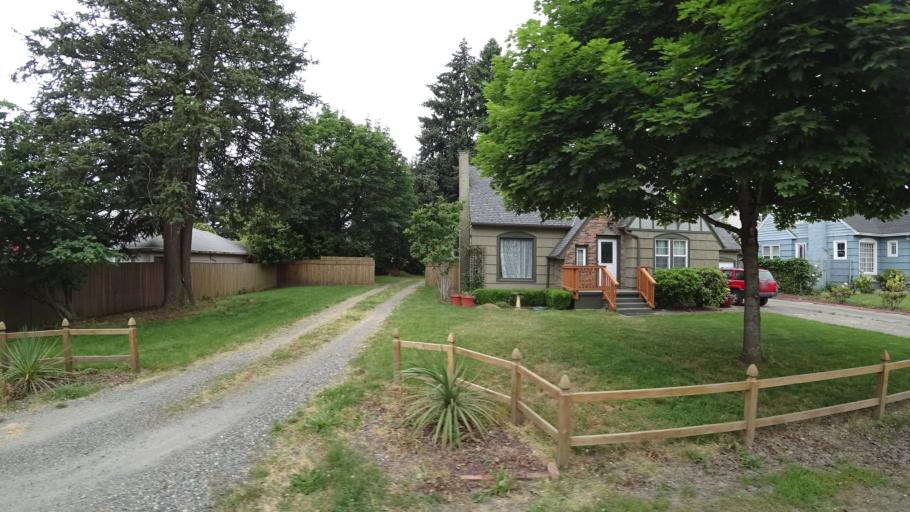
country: US
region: Oregon
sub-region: Multnomah County
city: Lents
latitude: 45.4978
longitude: -122.5395
